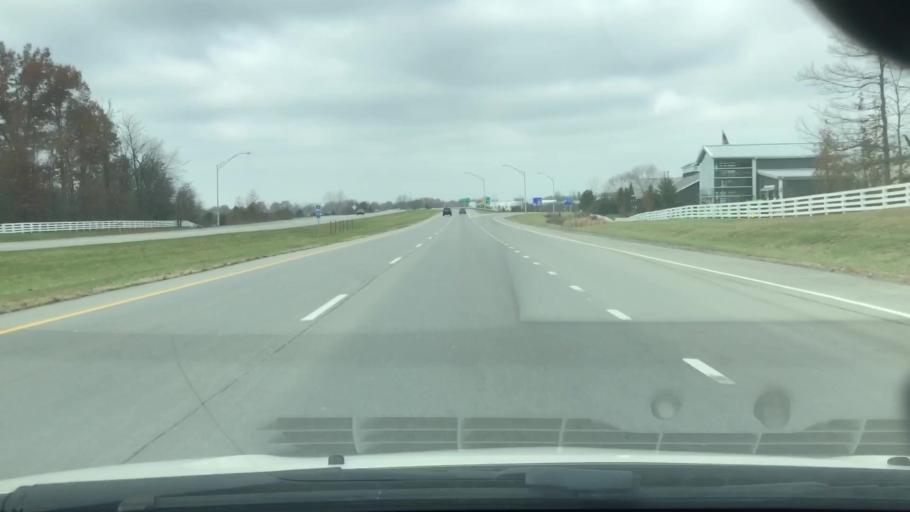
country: US
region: Ohio
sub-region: Franklin County
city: New Albany
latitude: 40.0846
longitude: -82.7943
